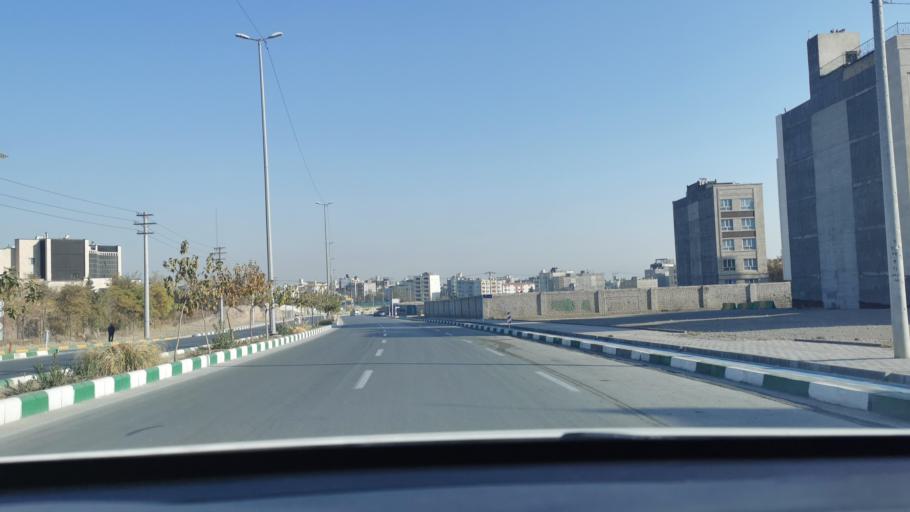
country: IR
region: Razavi Khorasan
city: Mashhad
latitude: 36.2787
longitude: 59.5411
